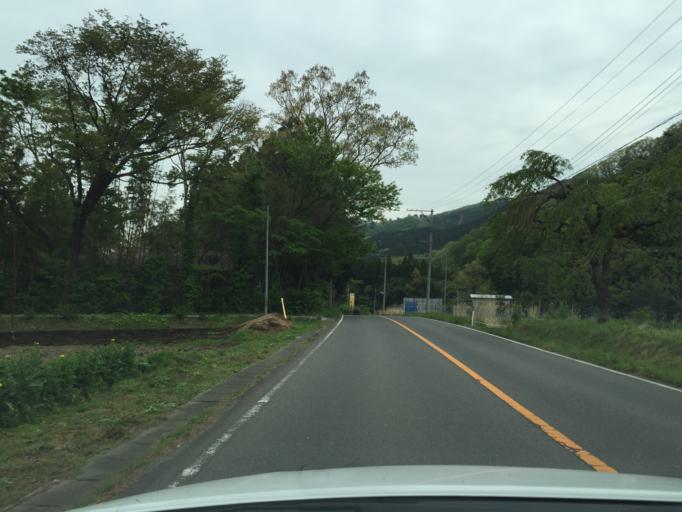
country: JP
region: Fukushima
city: Motomiya
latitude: 37.5153
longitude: 140.2700
